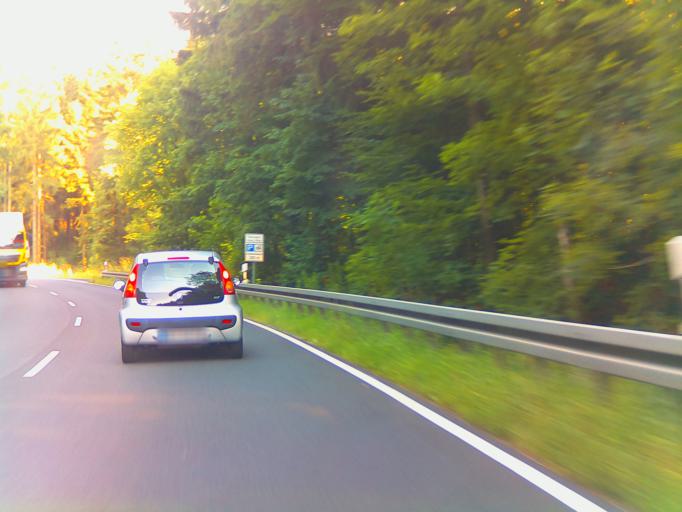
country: DE
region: Hesse
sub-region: Regierungsbezirk Kassel
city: Gersfeld
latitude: 50.4236
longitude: 9.9336
